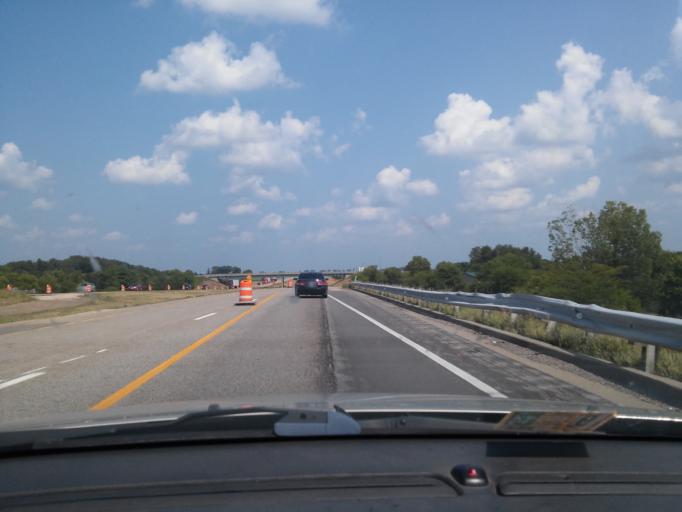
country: US
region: Illinois
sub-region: Logan County
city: Lincoln
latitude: 40.1815
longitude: -89.3624
